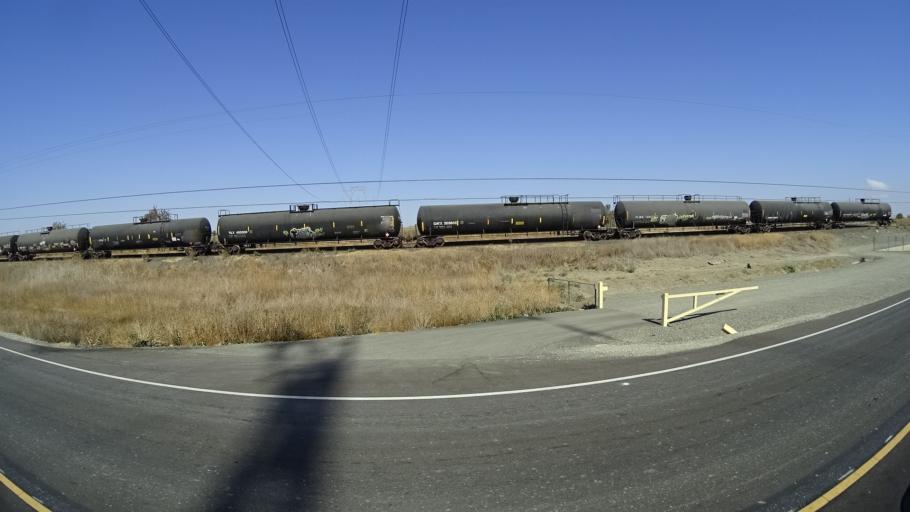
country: US
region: California
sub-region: Yolo County
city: Woodland
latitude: 38.6766
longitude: -121.6746
